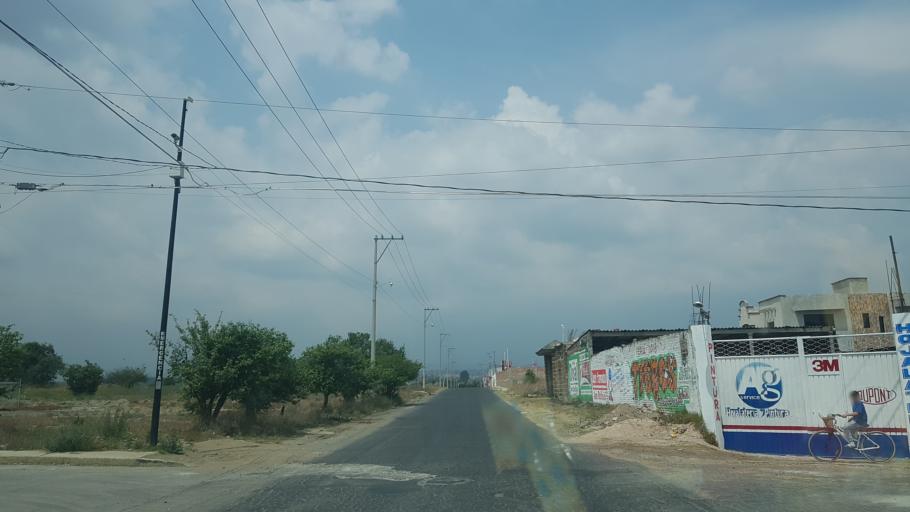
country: MX
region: Puebla
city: Huejotzingo
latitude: 19.1500
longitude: -98.4099
